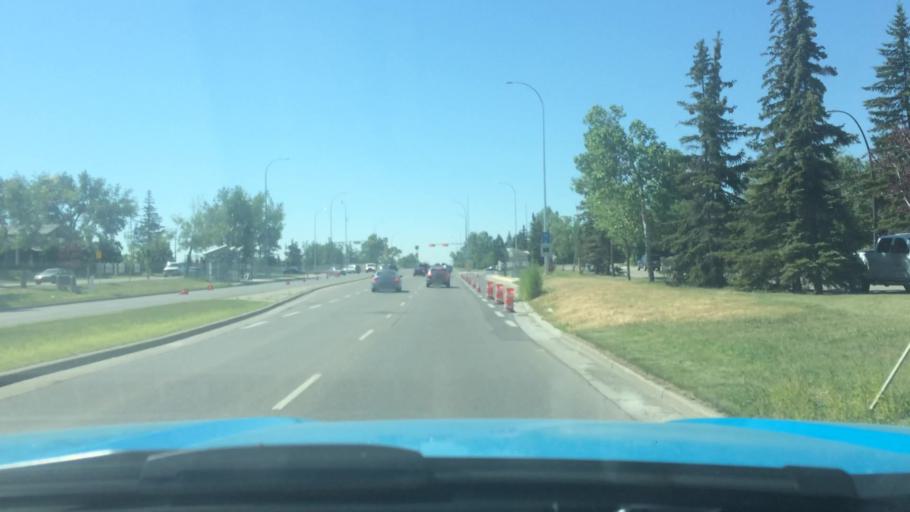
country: CA
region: Alberta
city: Calgary
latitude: 51.0831
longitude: -113.9584
